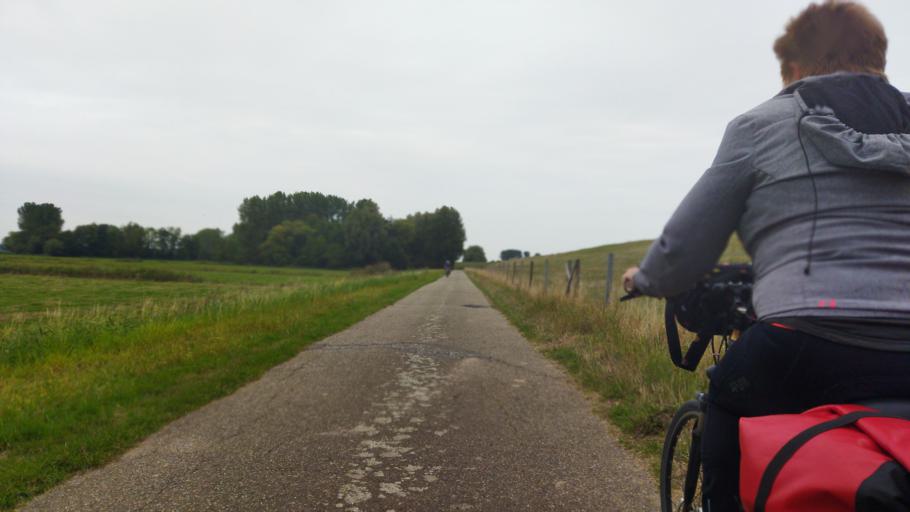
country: DE
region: Lower Saxony
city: Weener
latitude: 53.1236
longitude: 7.3729
